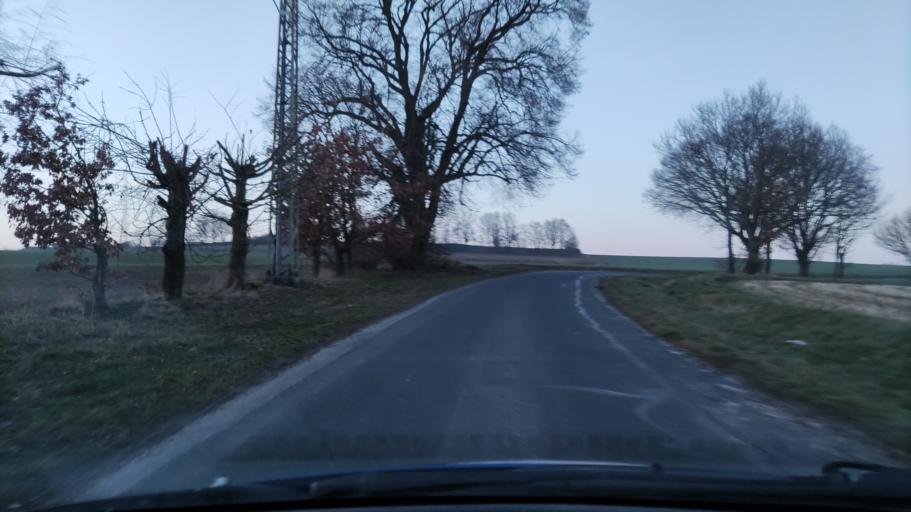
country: DE
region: Lower Saxony
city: Natendorf
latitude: 53.0477
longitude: 10.4781
